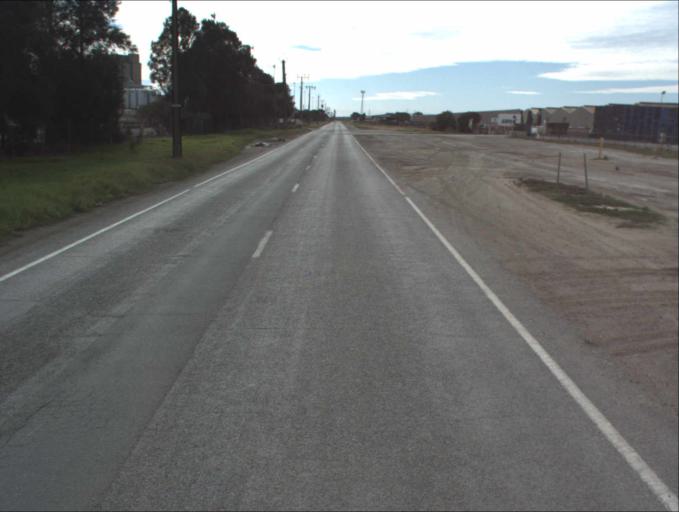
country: AU
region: South Australia
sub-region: Port Adelaide Enfield
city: Birkenhead
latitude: -34.8336
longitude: 138.5160
